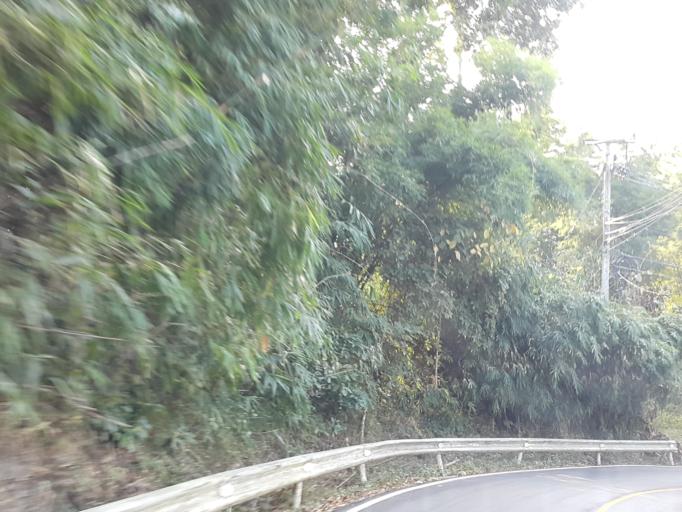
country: TH
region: Chiang Mai
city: Mae On
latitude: 18.8762
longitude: 99.2640
